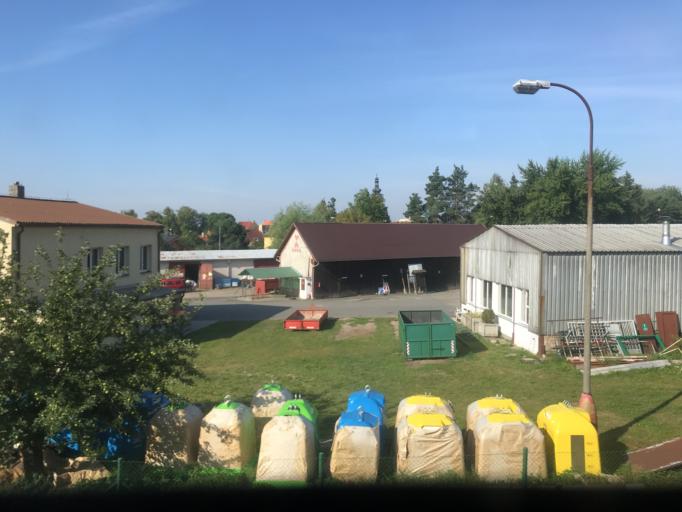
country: CZ
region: Jihocesky
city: Sobeslav
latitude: 49.2628
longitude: 14.7245
